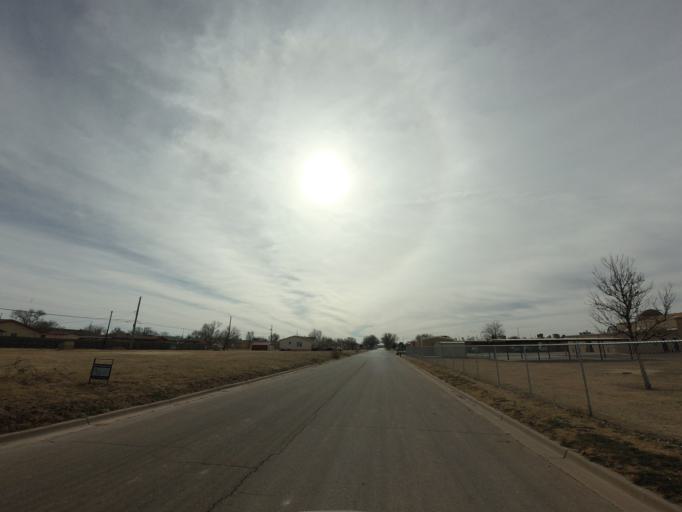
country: US
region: New Mexico
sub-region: Curry County
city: Clovis
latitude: 34.4114
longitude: -103.2405
